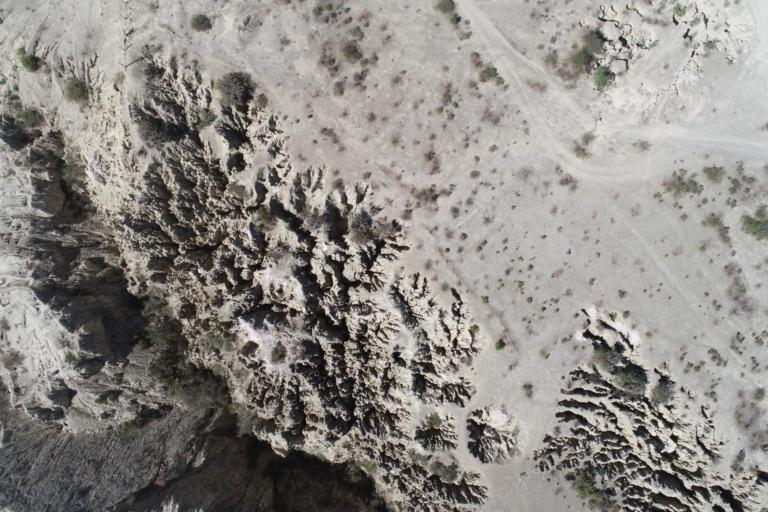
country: BO
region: La Paz
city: La Paz
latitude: -16.6363
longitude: -68.0512
